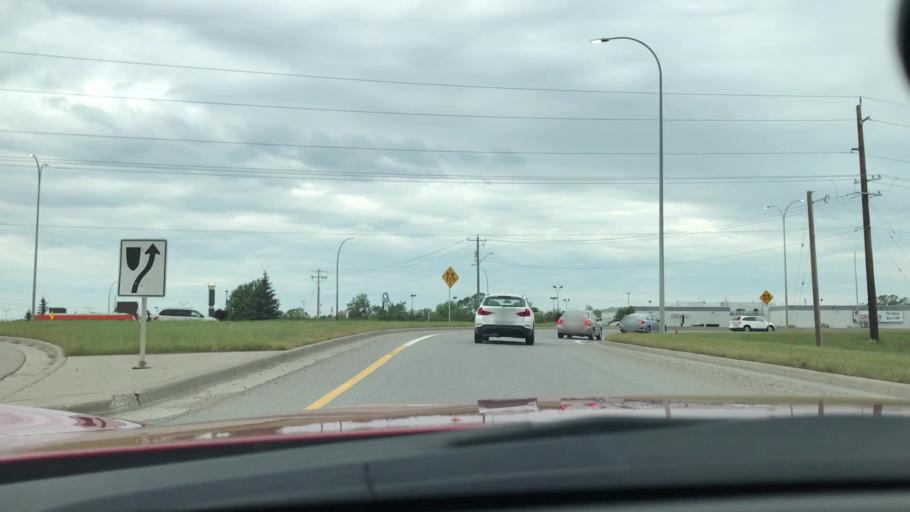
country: CA
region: Alberta
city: Calgary
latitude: 50.9895
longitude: -114.0266
